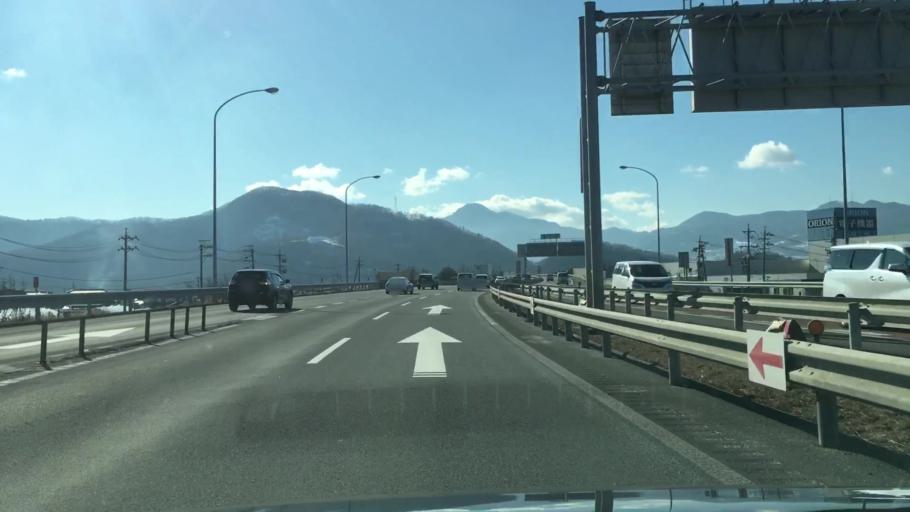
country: JP
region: Nagano
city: Nagano-shi
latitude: 36.5502
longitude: 138.1411
